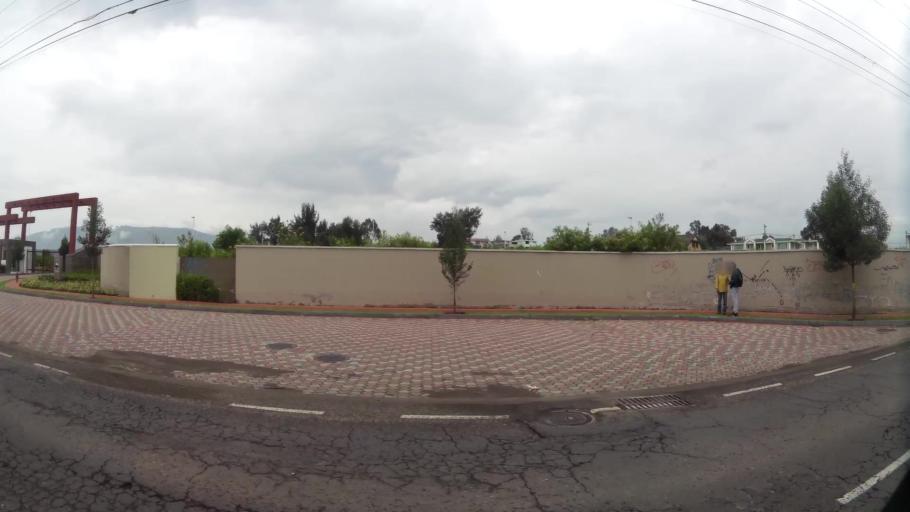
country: EC
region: Pichincha
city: Sangolqui
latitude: -0.3298
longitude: -78.4362
